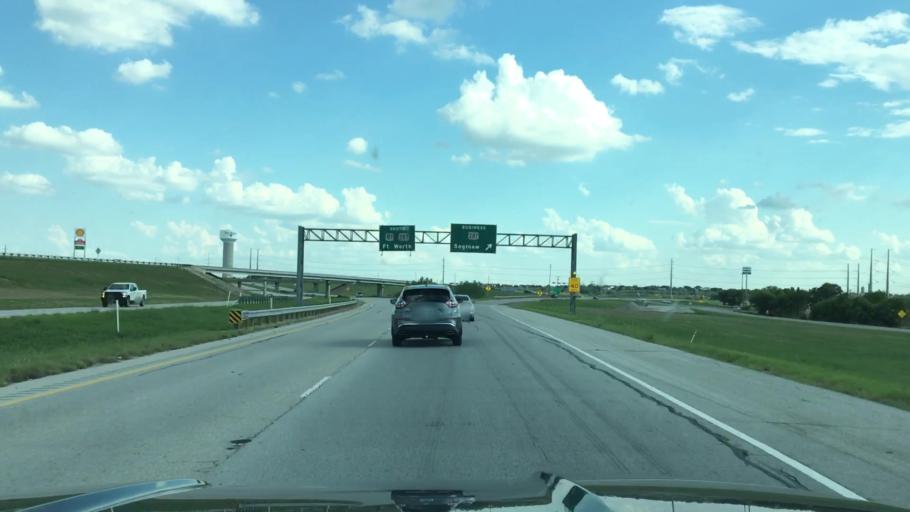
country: US
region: Texas
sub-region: Tarrant County
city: Pecan Acres
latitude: 32.9720
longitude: -97.4216
